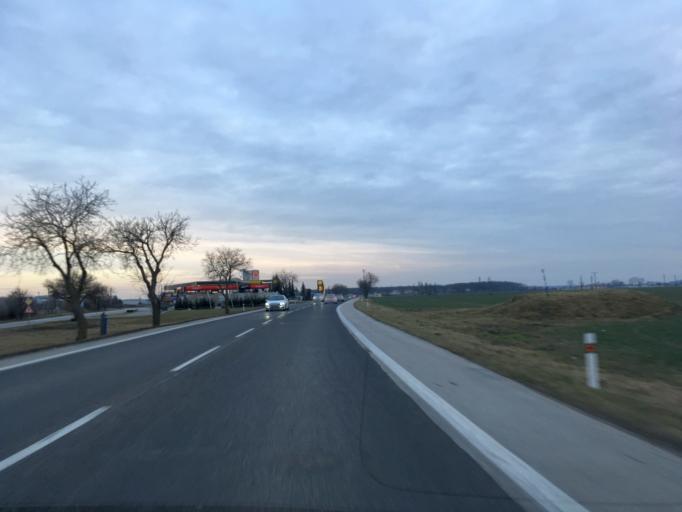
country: SK
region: Trnavsky
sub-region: Okres Dunajska Streda
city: Velky Meder
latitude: 47.8706
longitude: 17.7576
